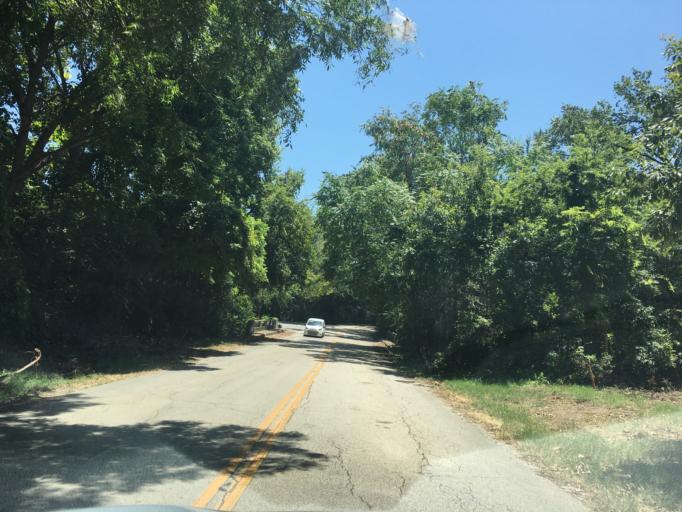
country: US
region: Texas
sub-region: Dallas County
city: Highland Park
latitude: 32.8356
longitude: -96.7405
